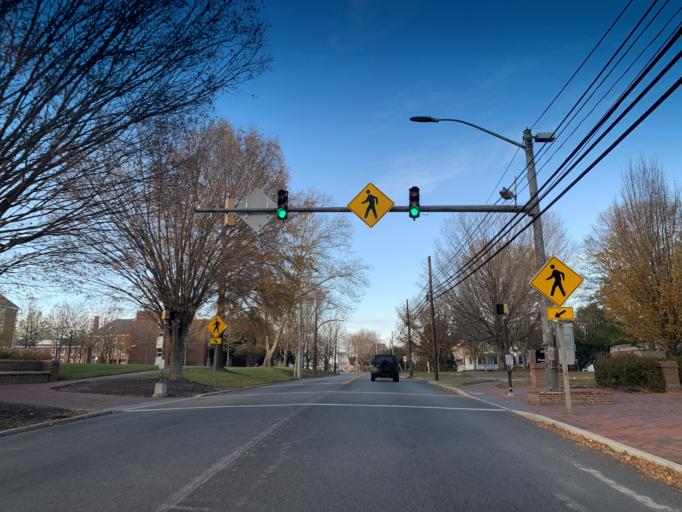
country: US
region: Maryland
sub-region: Kent County
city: Chestertown
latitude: 39.2176
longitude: -76.0669
